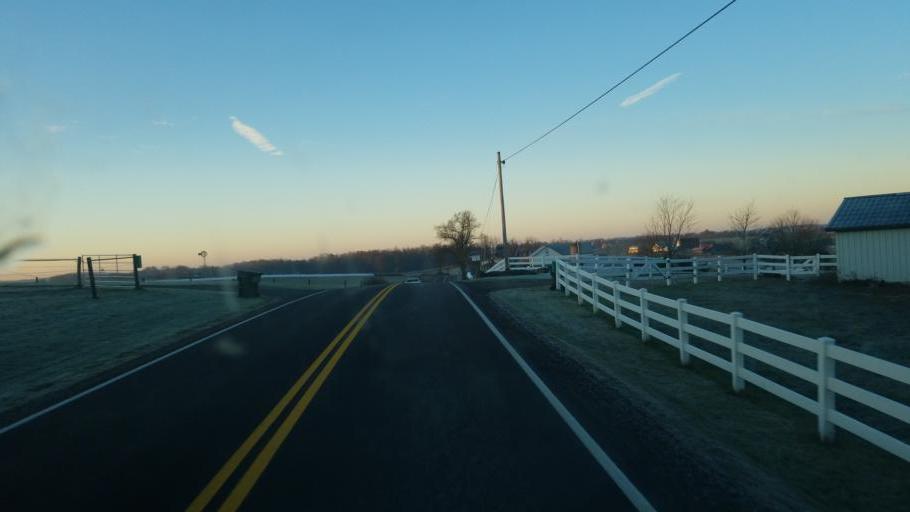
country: US
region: Ohio
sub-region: Wayne County
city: Apple Creek
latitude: 40.7078
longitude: -81.8356
